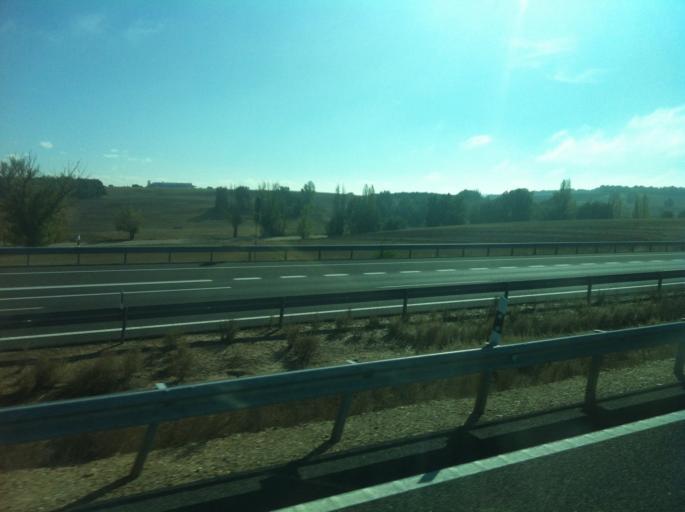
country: ES
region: Castille and Leon
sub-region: Provincia de Burgos
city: Valdorros
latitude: 42.1485
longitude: -3.7033
